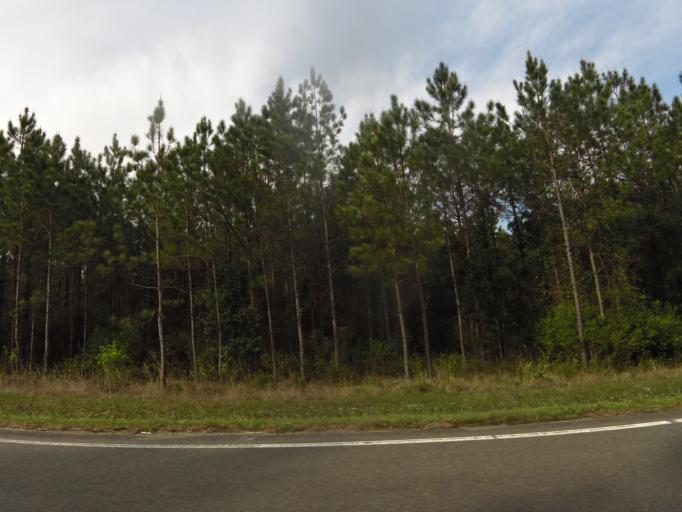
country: US
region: Georgia
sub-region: Camden County
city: Kingsland
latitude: 30.6956
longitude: -81.7157
